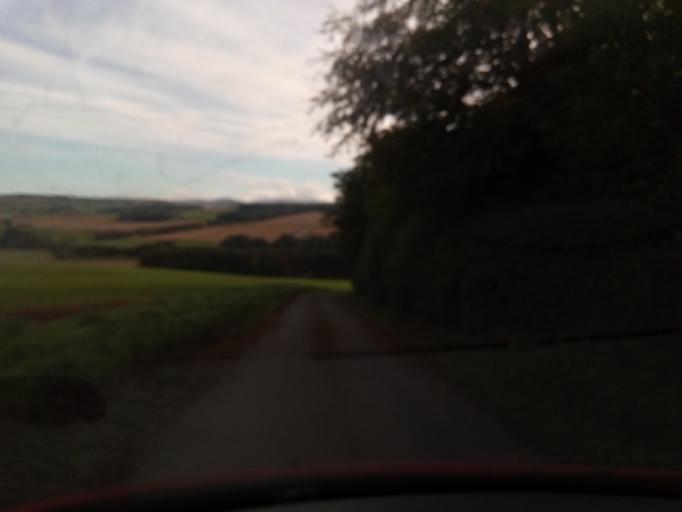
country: GB
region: Scotland
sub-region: The Scottish Borders
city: Jedburgh
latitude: 55.4813
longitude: -2.4973
